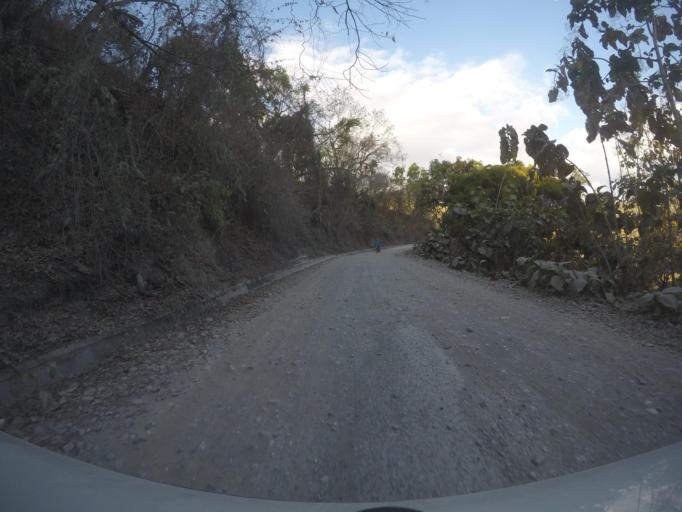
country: ID
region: East Nusa Tenggara
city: Atambua
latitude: -8.9624
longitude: 125.0229
